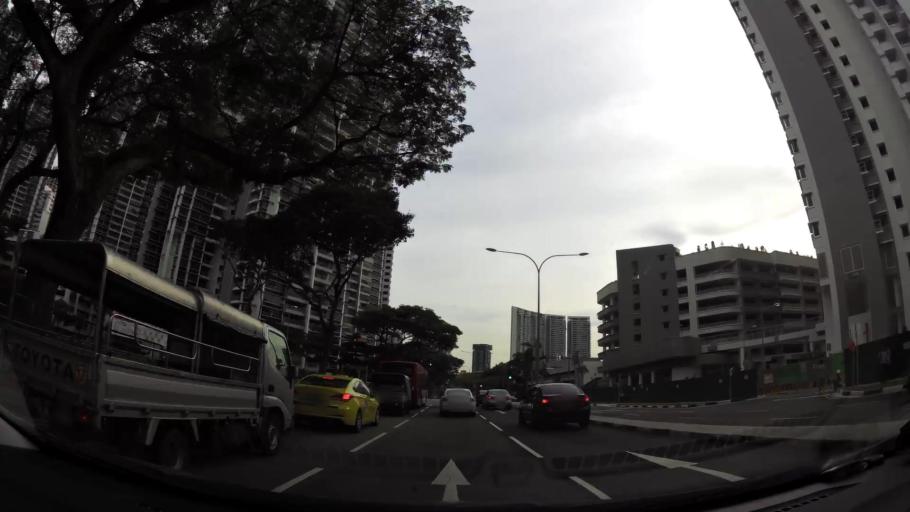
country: SG
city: Singapore
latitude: 1.3375
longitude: 103.8438
